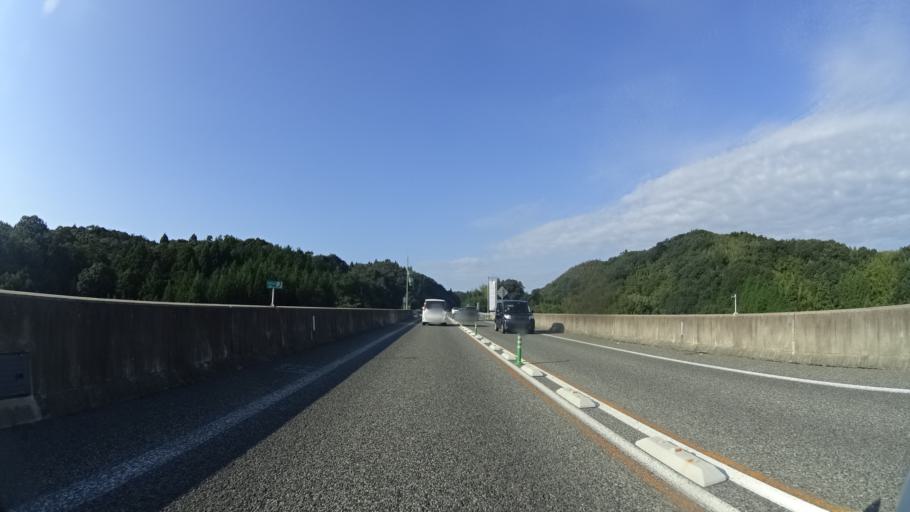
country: JP
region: Shimane
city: Hiratacho
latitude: 35.4024
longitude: 132.9280
